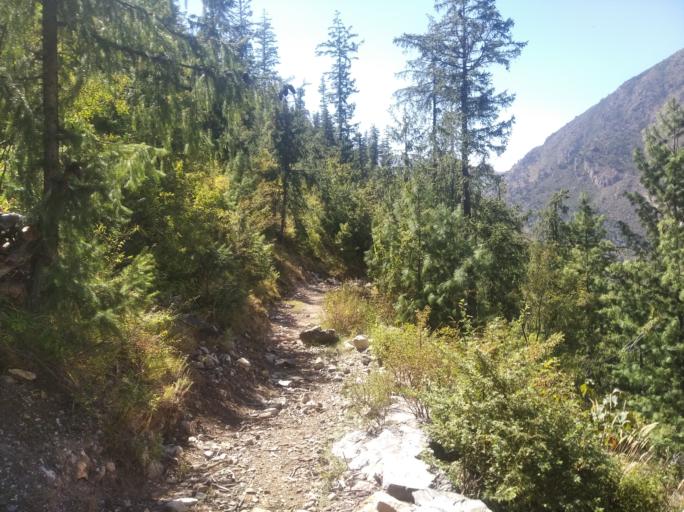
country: NP
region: Western Region
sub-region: Dhawalagiri Zone
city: Jomsom
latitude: 28.8859
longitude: 83.0363
